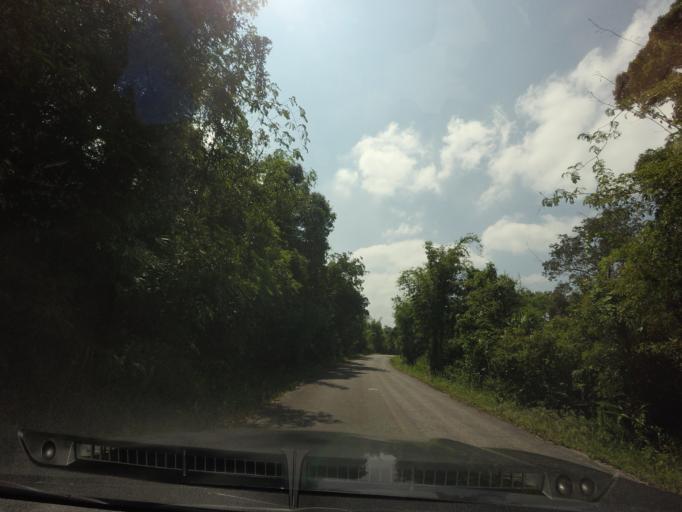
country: TH
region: Loei
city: Na Haeo
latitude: 17.4953
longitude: 100.9389
